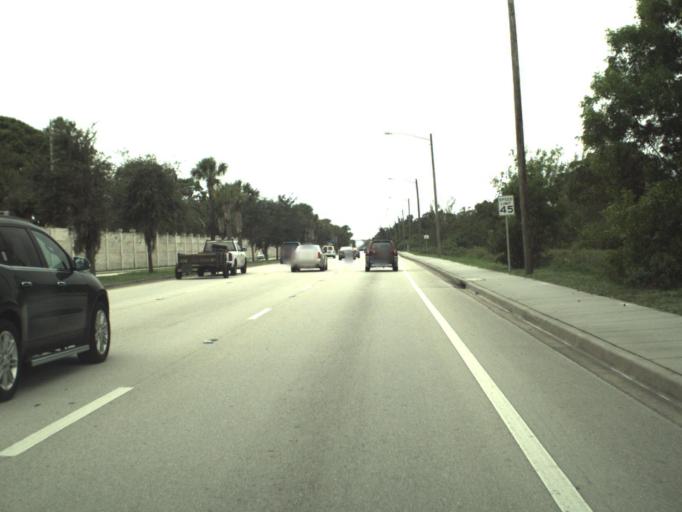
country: US
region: Florida
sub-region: Palm Beach County
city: Mangonia Park
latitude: 26.7538
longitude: -80.1091
